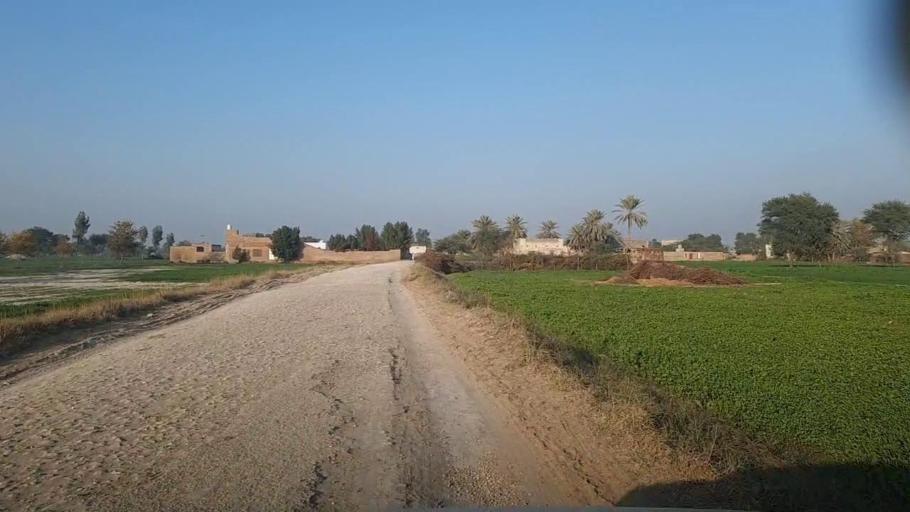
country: PK
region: Sindh
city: Khairpur
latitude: 28.0741
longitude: 69.7448
